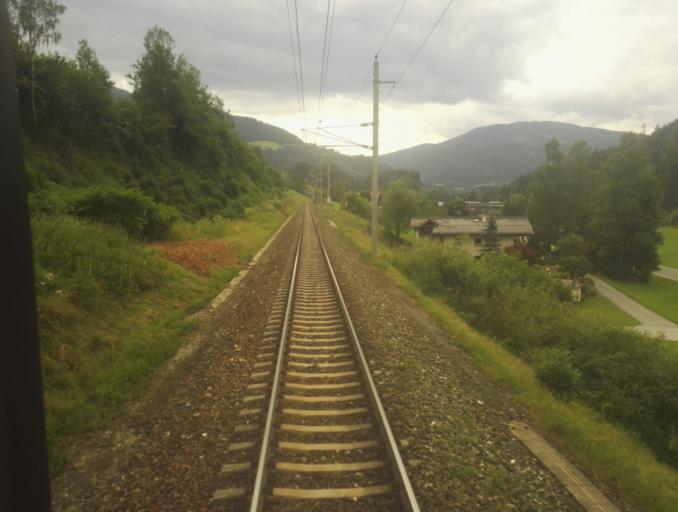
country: AT
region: Salzburg
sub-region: Politischer Bezirk Sankt Johann im Pongau
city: Eben im Pongau
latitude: 47.4215
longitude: 13.3552
